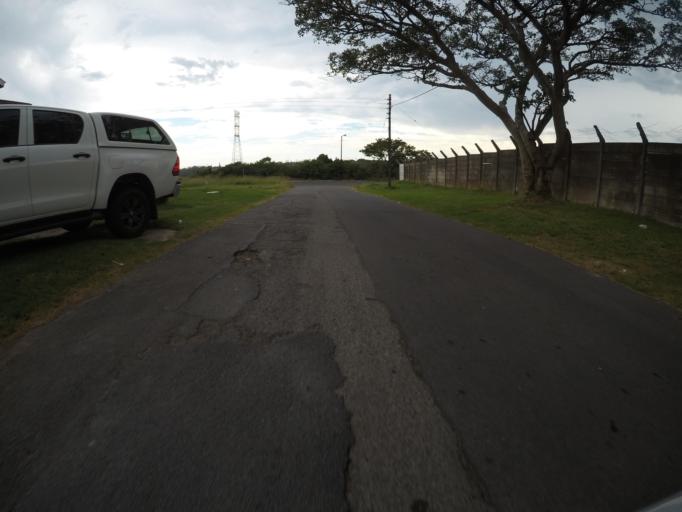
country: ZA
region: Eastern Cape
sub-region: Buffalo City Metropolitan Municipality
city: East London
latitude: -33.0247
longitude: 27.8642
